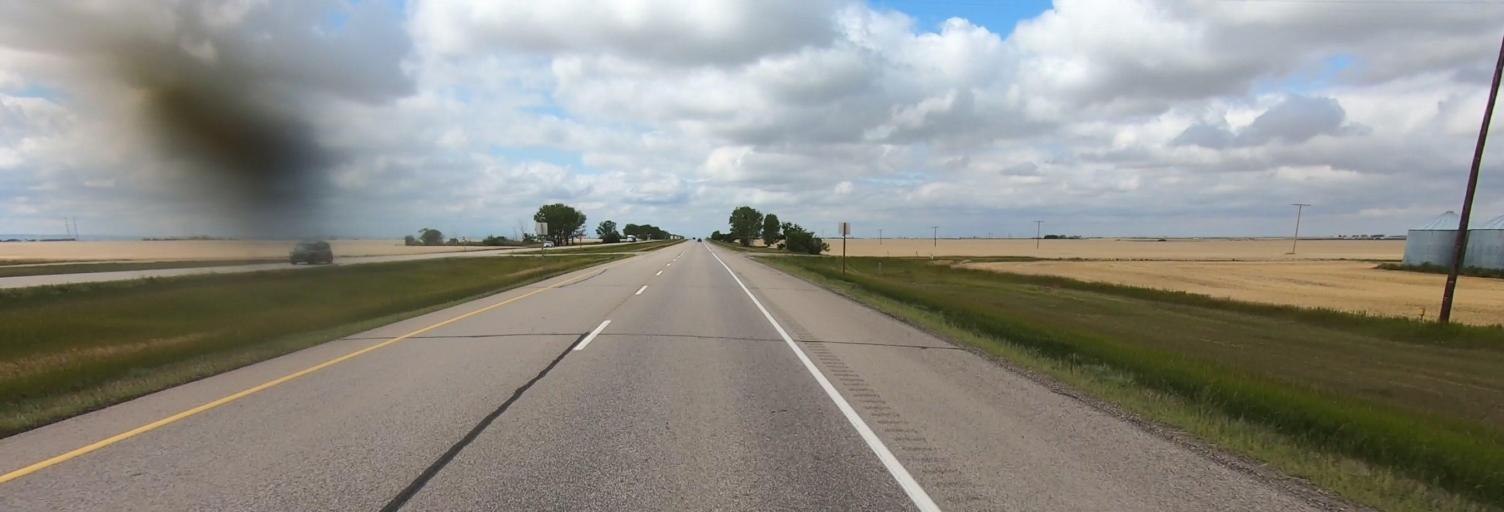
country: CA
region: Saskatchewan
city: Moose Jaw
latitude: 50.3957
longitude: -105.3253
